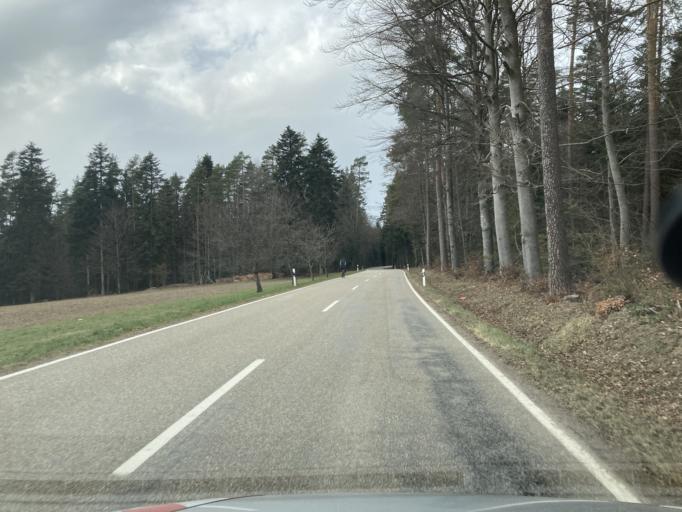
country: DE
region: Baden-Wuerttemberg
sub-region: Karlsruhe Region
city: Neuweiler
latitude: 48.6668
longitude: 8.6244
